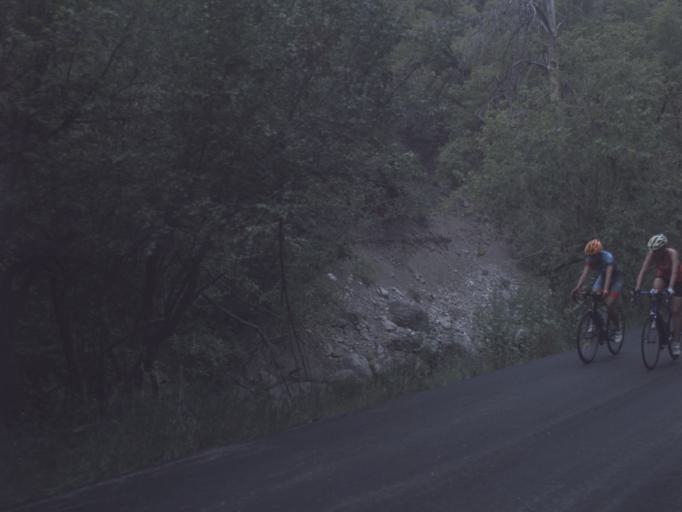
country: US
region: Utah
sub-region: Utah County
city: Cedar Hills
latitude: 40.4484
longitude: -111.6787
